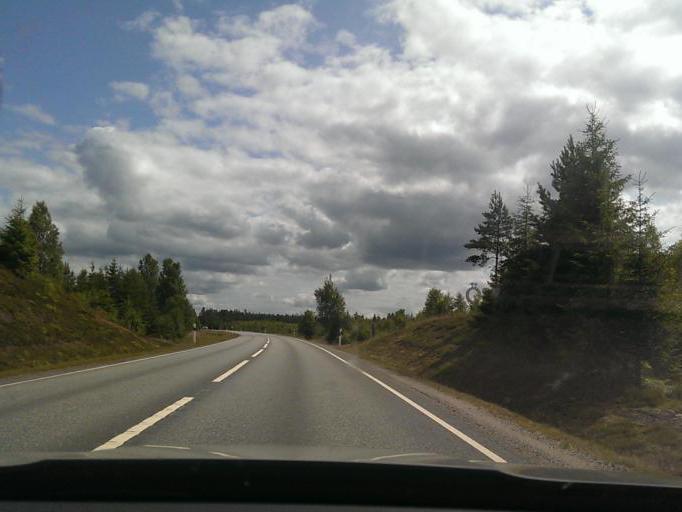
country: SE
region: Joenkoeping
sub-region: Varnamo Kommun
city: Varnamo
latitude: 57.2666
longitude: 13.9716
